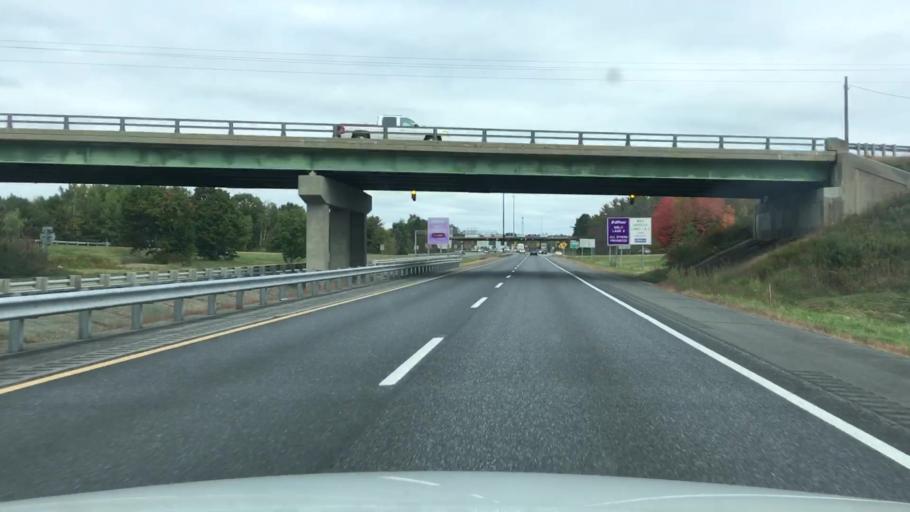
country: US
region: Maine
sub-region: Kennebec County
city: Gardiner
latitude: 44.2091
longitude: -69.8246
